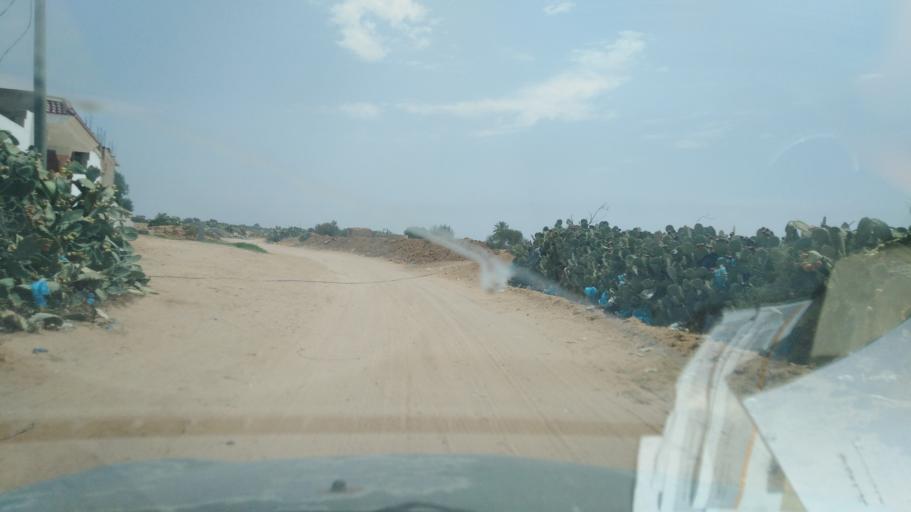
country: TN
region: Safaqis
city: Sfax
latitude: 34.7388
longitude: 10.5447
